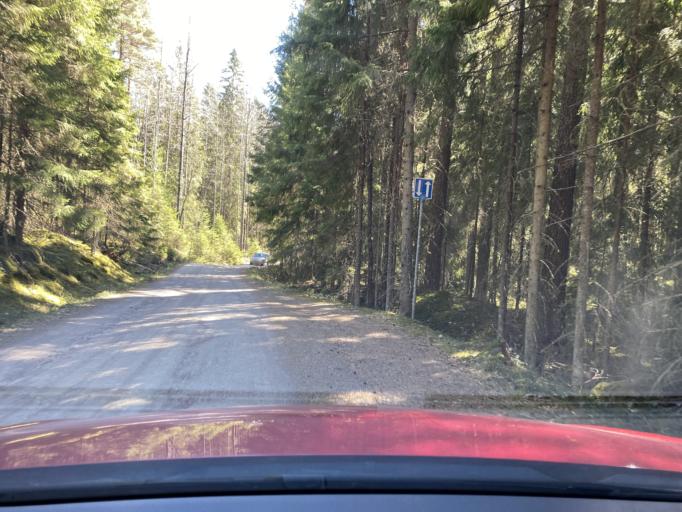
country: FI
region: Uusimaa
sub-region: Helsinki
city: Kaerkoelae
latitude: 60.6589
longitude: 23.8692
